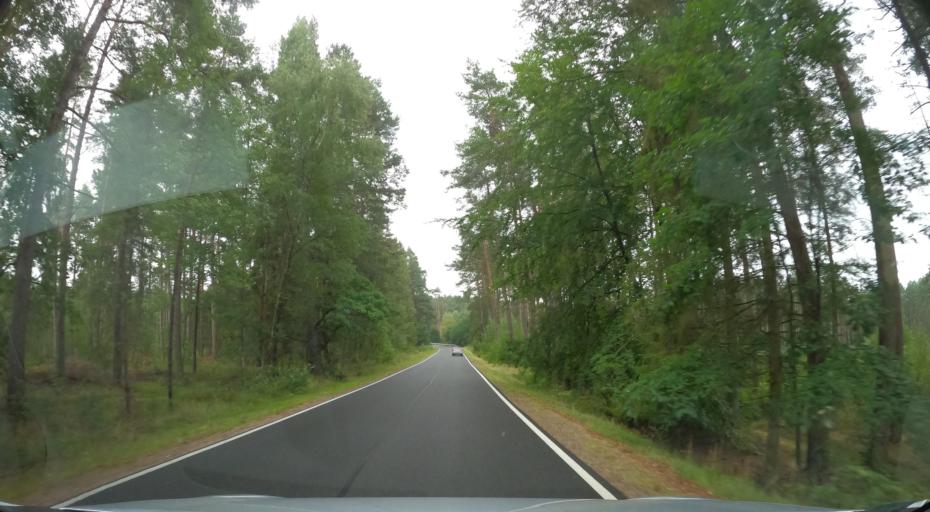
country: PL
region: Pomeranian Voivodeship
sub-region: Powiat wejherowski
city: Linia
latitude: 54.4875
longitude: 17.8440
